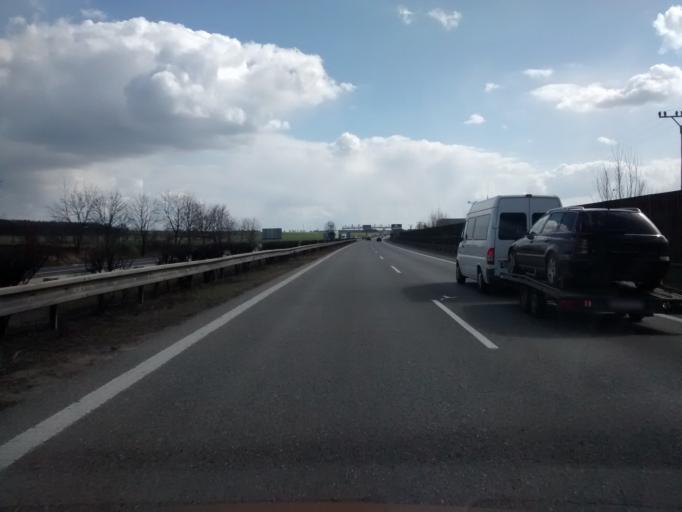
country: CZ
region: Central Bohemia
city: Zdiby
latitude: 50.2013
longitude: 14.4387
